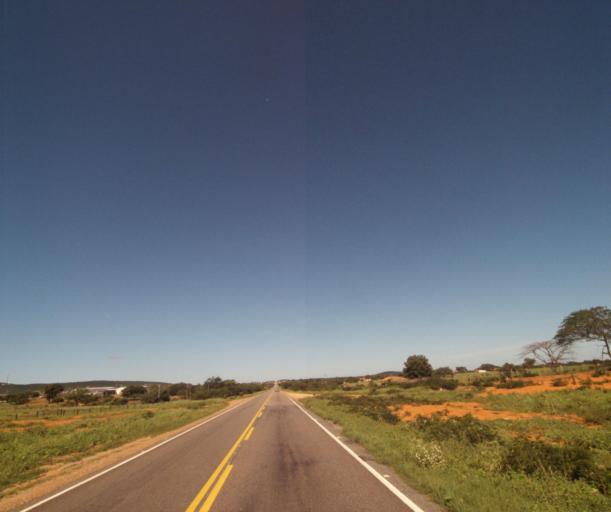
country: BR
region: Bahia
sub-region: Palmas De Monte Alto
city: Palmas de Monte Alto
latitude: -14.2481
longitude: -43.1458
